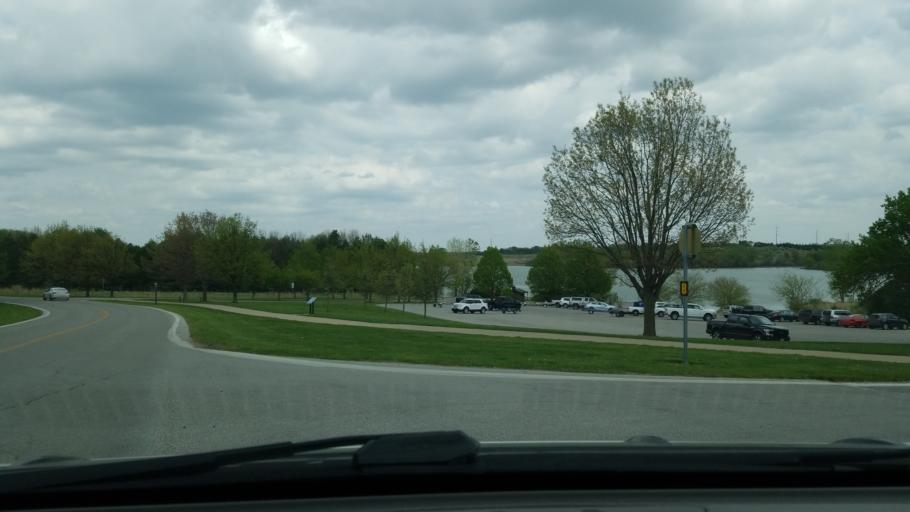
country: US
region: Nebraska
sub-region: Sarpy County
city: Chalco
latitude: 41.1651
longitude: -96.1575
